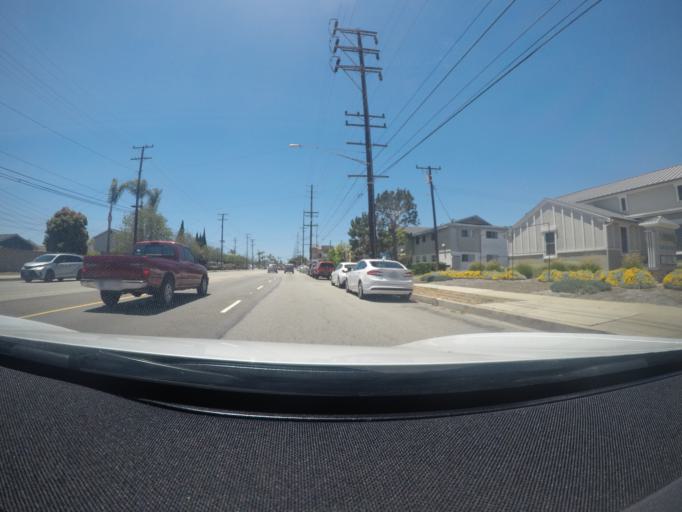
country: US
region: California
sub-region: Los Angeles County
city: Torrance
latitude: 33.8583
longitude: -118.3591
